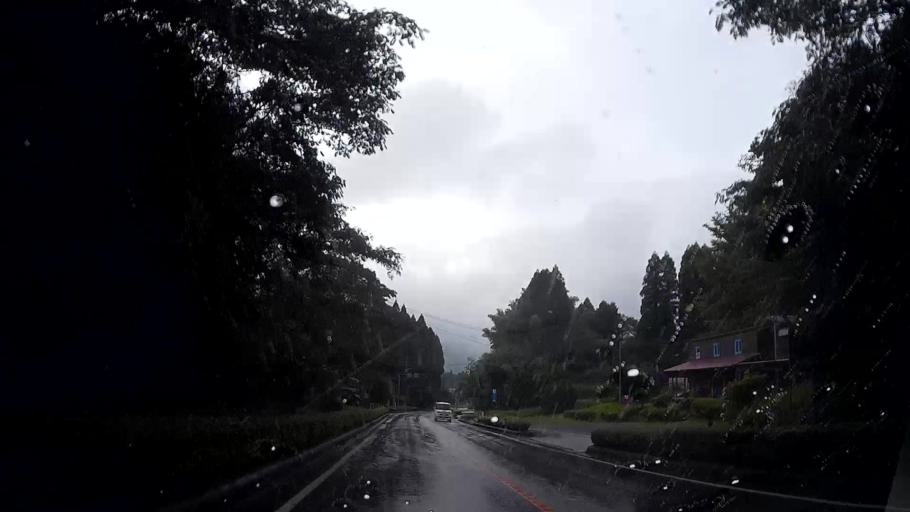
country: JP
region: Kumamoto
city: Aso
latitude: 32.8593
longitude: 131.0052
